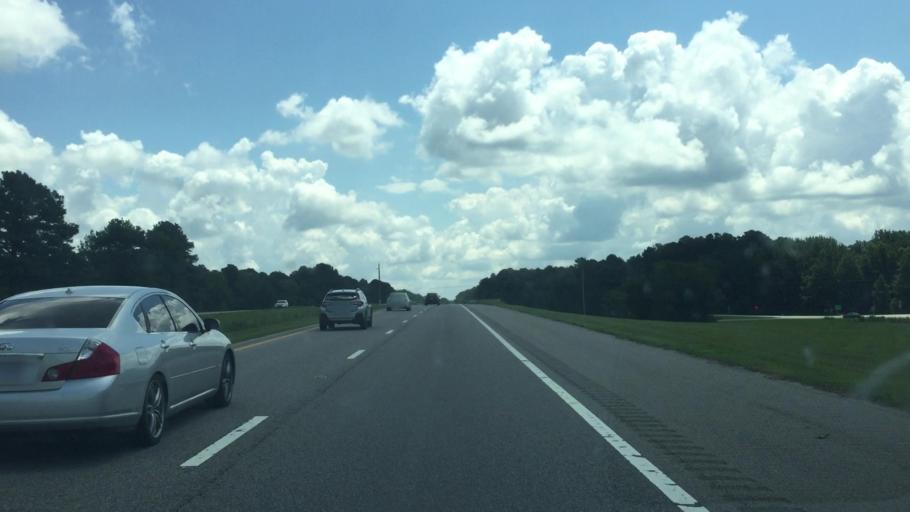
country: US
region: North Carolina
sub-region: Robeson County
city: Lumberton
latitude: 34.5808
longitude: -79.0505
